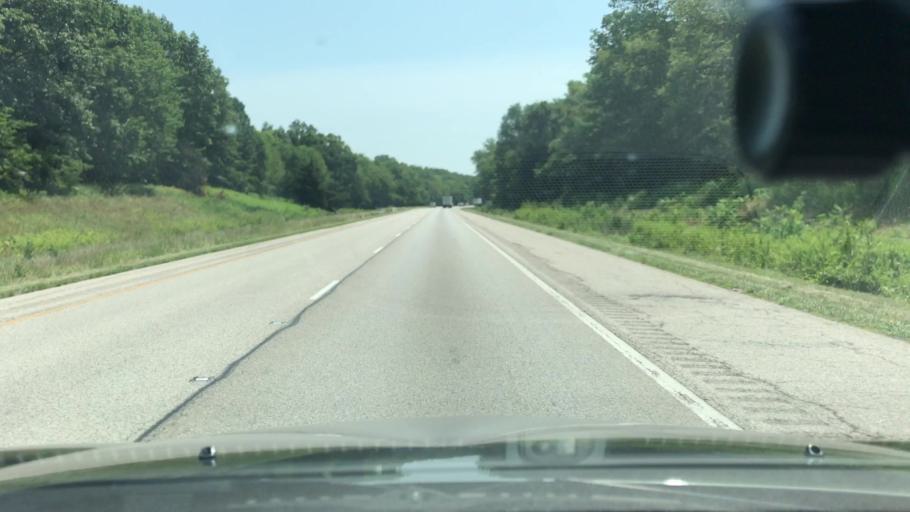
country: US
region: Illinois
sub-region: Washington County
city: Nashville
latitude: 38.4083
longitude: -89.4165
